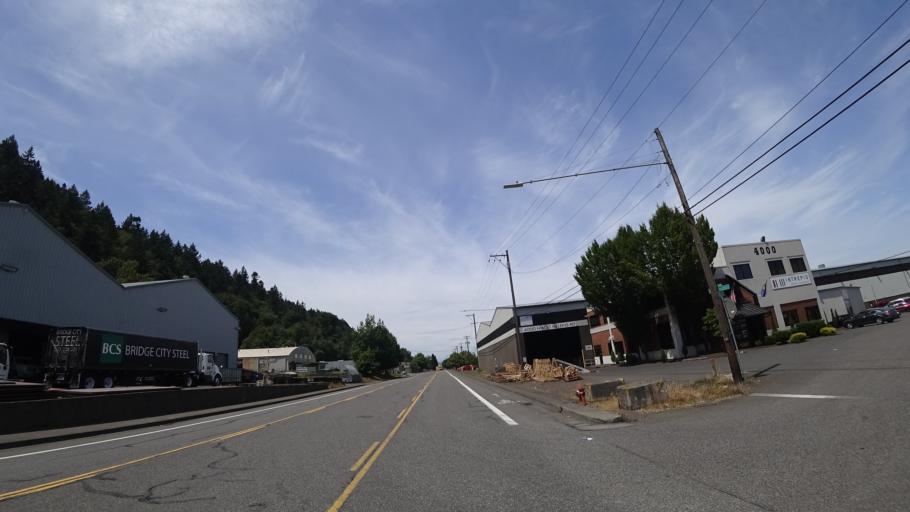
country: US
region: Oregon
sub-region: Washington County
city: West Haven-Sylvan
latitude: 45.5502
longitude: -122.7283
